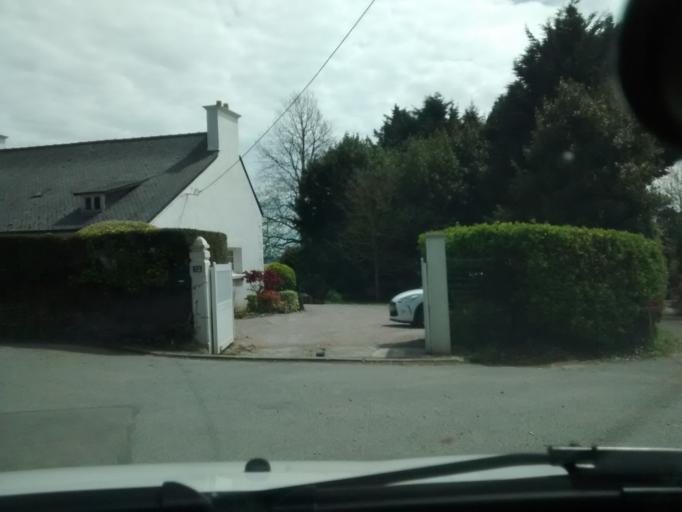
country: FR
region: Brittany
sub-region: Departement des Cotes-d'Armor
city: Ploubazlanec
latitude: 48.7973
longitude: -3.0227
